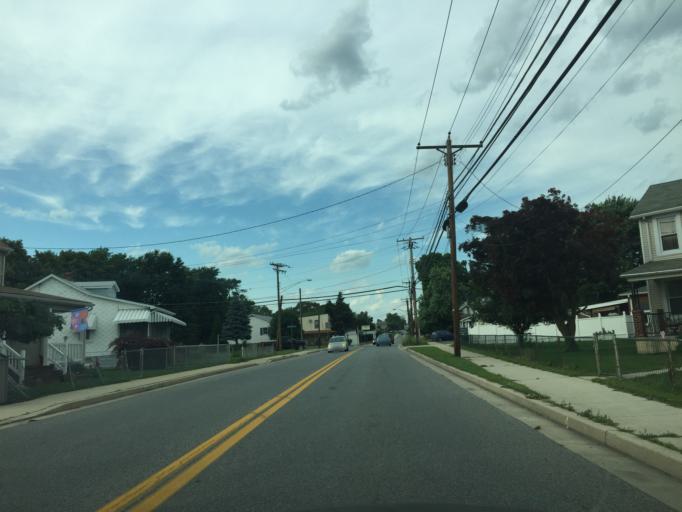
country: US
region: Maryland
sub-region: Baltimore County
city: Essex
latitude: 39.3097
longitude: -76.4785
